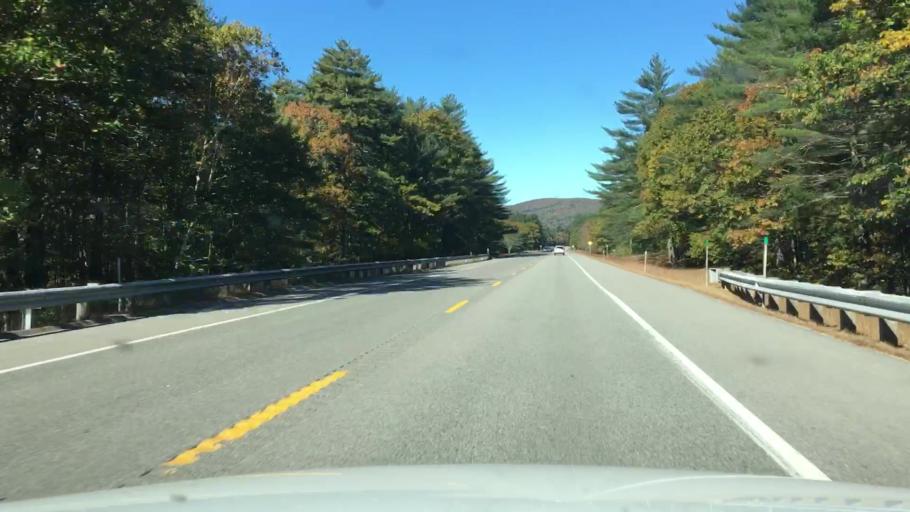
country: US
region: New Hampshire
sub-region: Carroll County
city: Sanbornville
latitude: 43.4913
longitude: -71.0163
